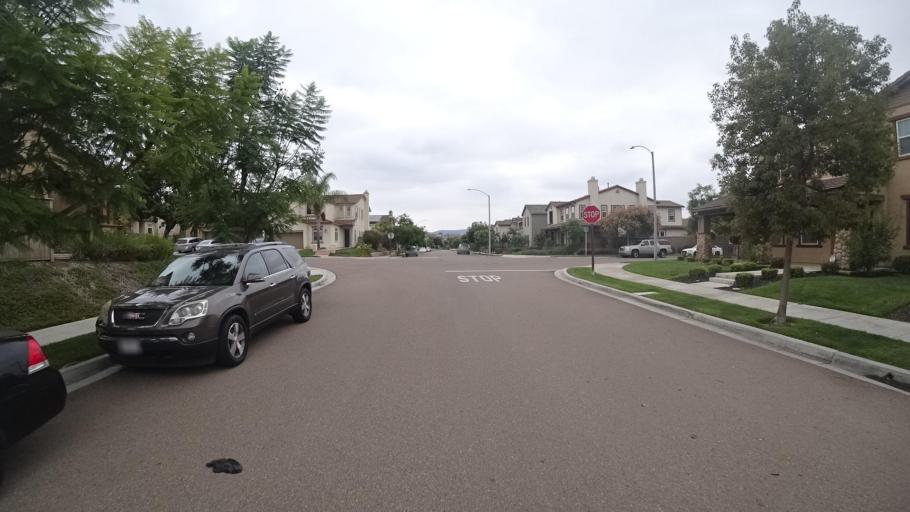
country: US
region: California
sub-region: San Diego County
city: Fairbanks Ranch
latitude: 33.0300
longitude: -117.1099
